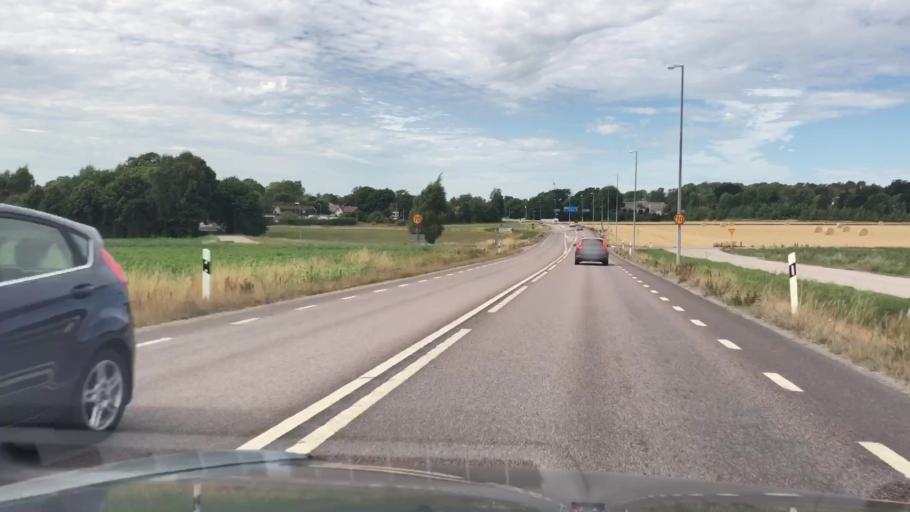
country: SE
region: Blekinge
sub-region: Karlskrona Kommun
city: Jaemjoe
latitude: 56.1845
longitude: 15.7736
